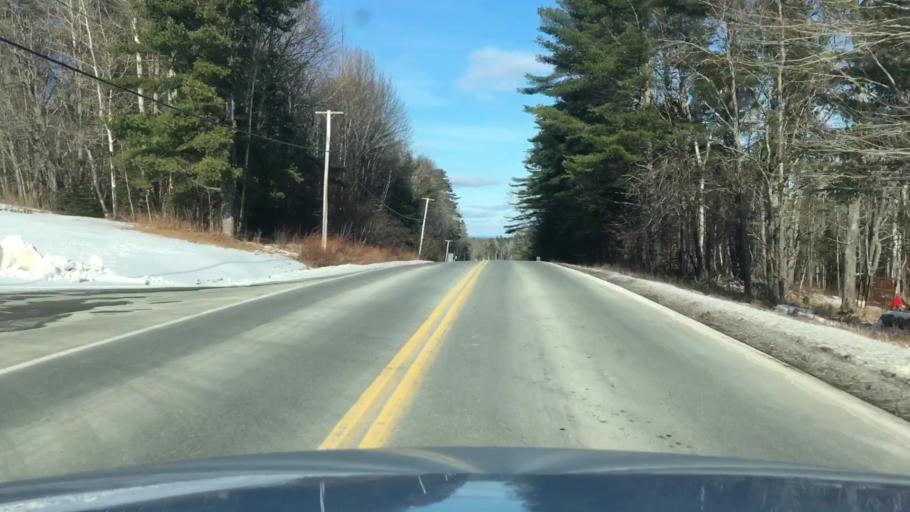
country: US
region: Maine
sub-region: Penobscot County
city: Holden
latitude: 44.7454
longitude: -68.6153
